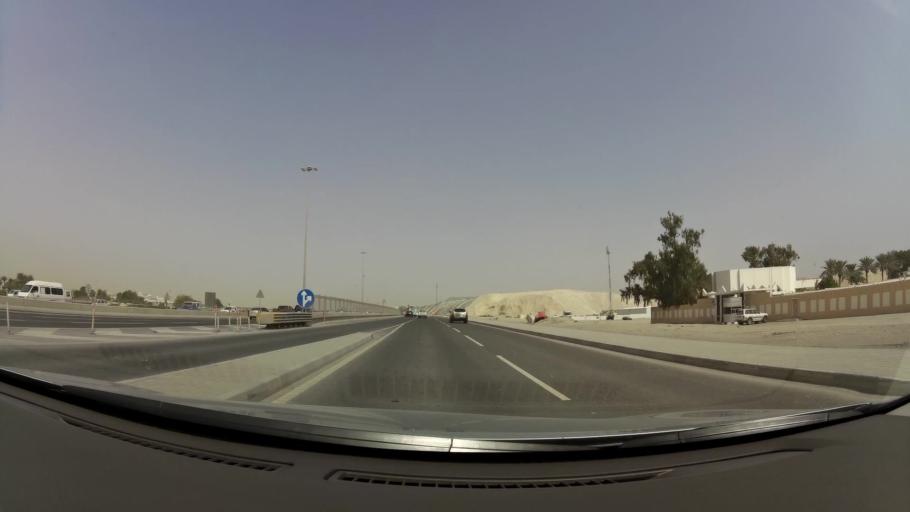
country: QA
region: Baladiyat ad Dawhah
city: Doha
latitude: 25.2857
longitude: 51.4825
